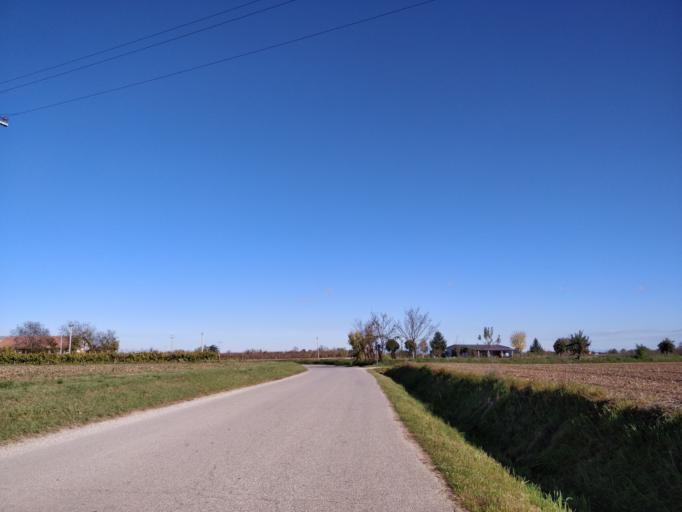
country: IT
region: Friuli Venezia Giulia
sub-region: Provincia di Udine
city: Bertiolo
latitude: 45.9388
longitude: 13.0519
